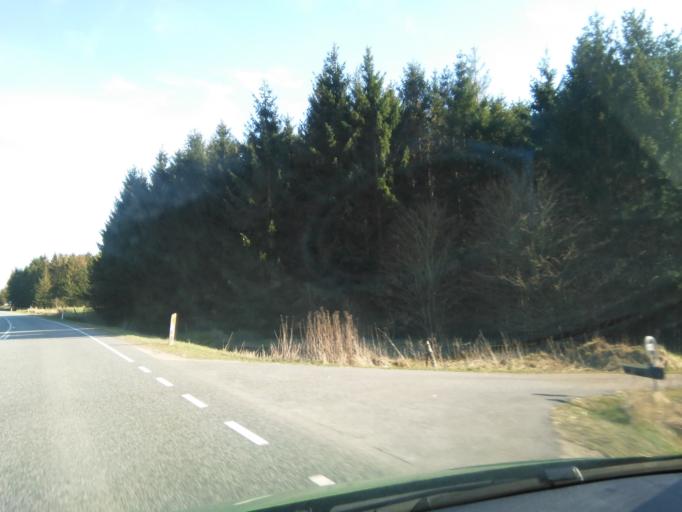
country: DK
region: Central Jutland
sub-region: Horsens Kommune
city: Braedstrup
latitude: 55.9010
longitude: 9.6115
